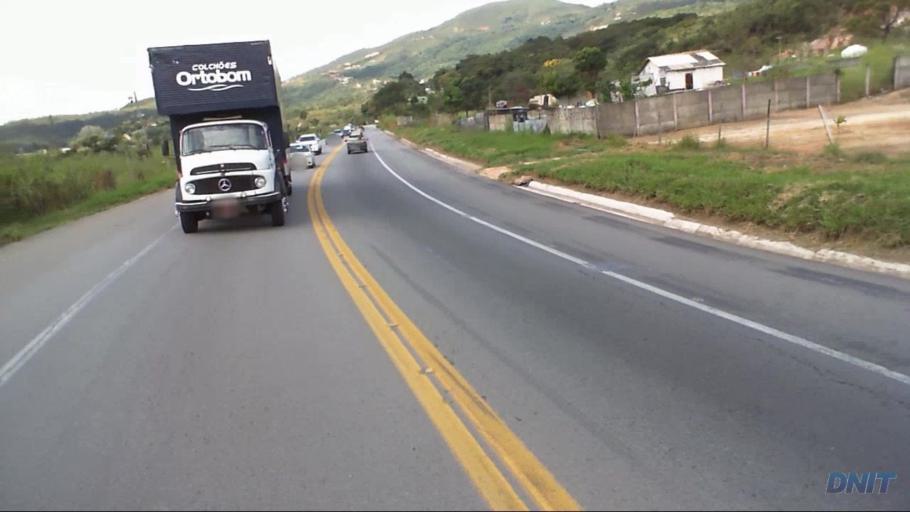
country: BR
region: Minas Gerais
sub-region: Santa Luzia
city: Santa Luzia
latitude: -19.8153
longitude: -43.8094
